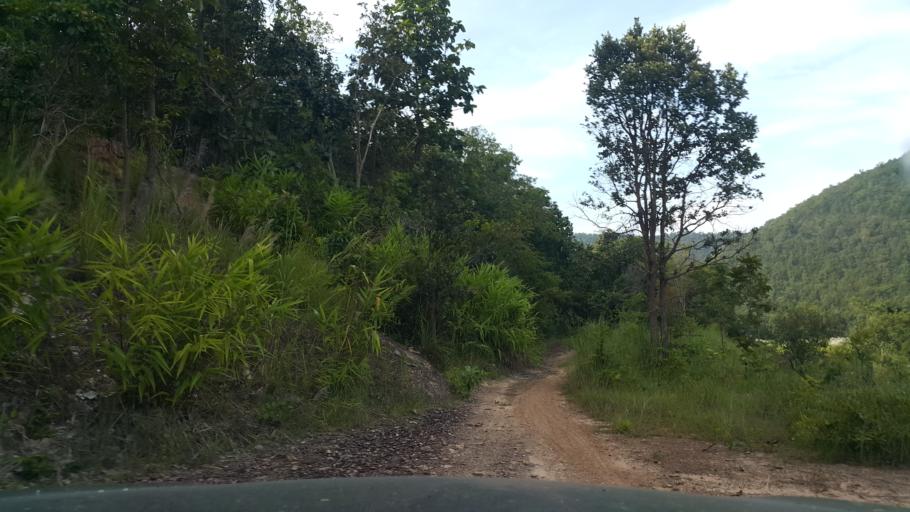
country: TH
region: Chiang Mai
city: San Sai
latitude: 18.9218
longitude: 99.0943
